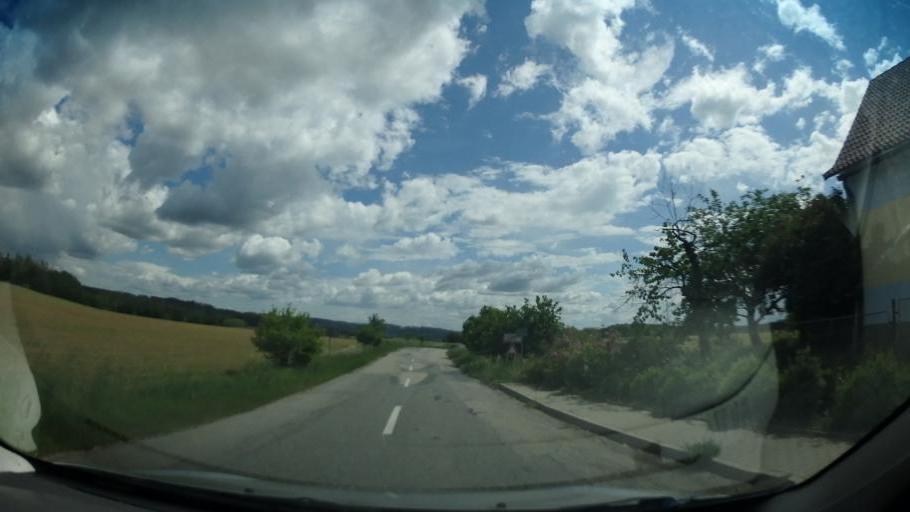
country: CZ
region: South Moravian
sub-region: Okres Blansko
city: Letovice
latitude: 49.5916
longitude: 16.5950
